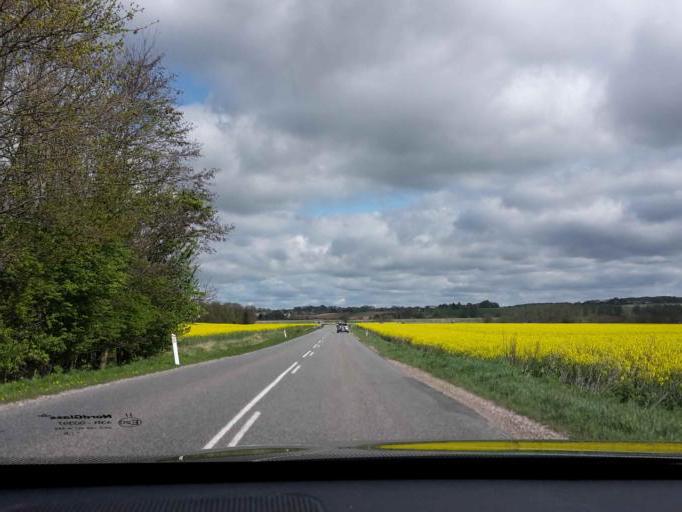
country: DK
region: Central Jutland
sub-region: Syddjurs Kommune
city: Hornslet
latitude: 56.3370
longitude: 10.3357
